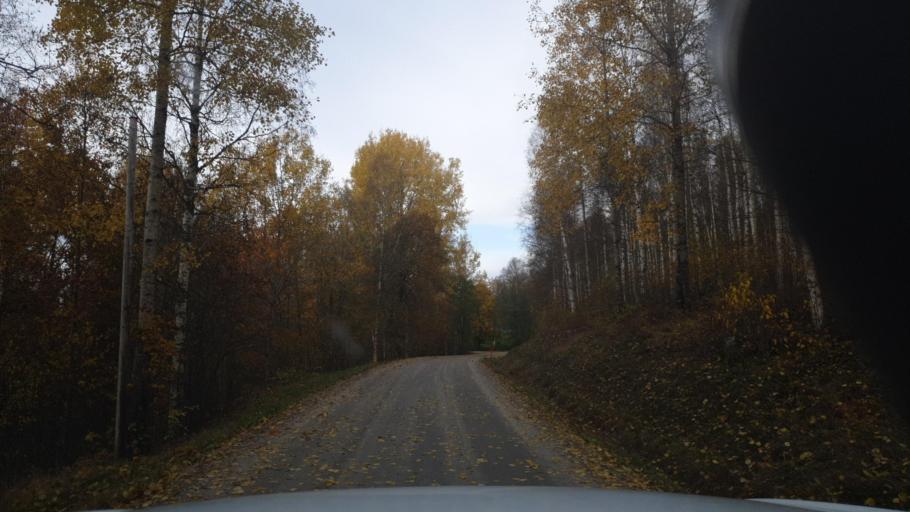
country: SE
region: Vaermland
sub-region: Arvika Kommun
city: Arvika
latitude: 59.7145
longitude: 12.8469
